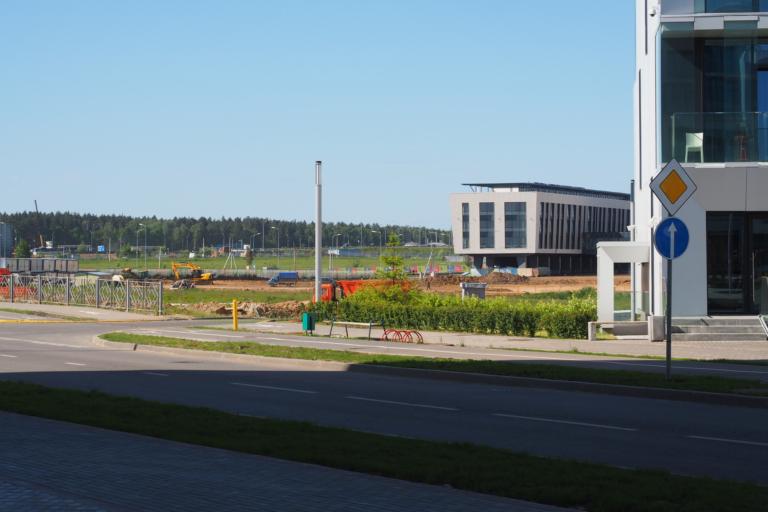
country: RU
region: Moskovskaya
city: Novoivanovskoye
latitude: 55.6933
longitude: 37.3513
